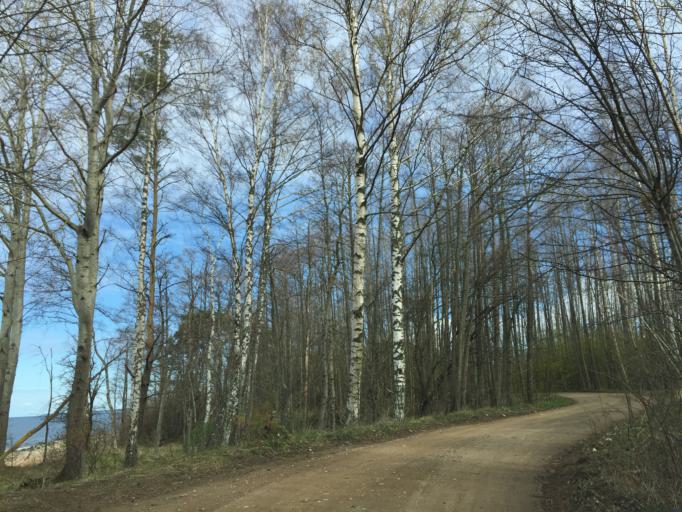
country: LV
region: Salacgrivas
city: Salacgriva
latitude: 57.5873
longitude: 24.3698
